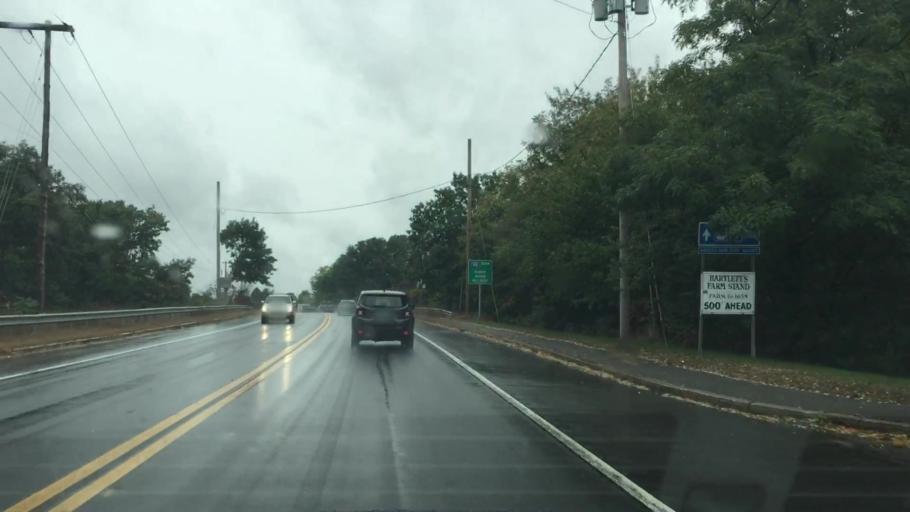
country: US
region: New Hampshire
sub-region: Rockingham County
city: Seabrook
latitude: 42.8683
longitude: -70.8882
